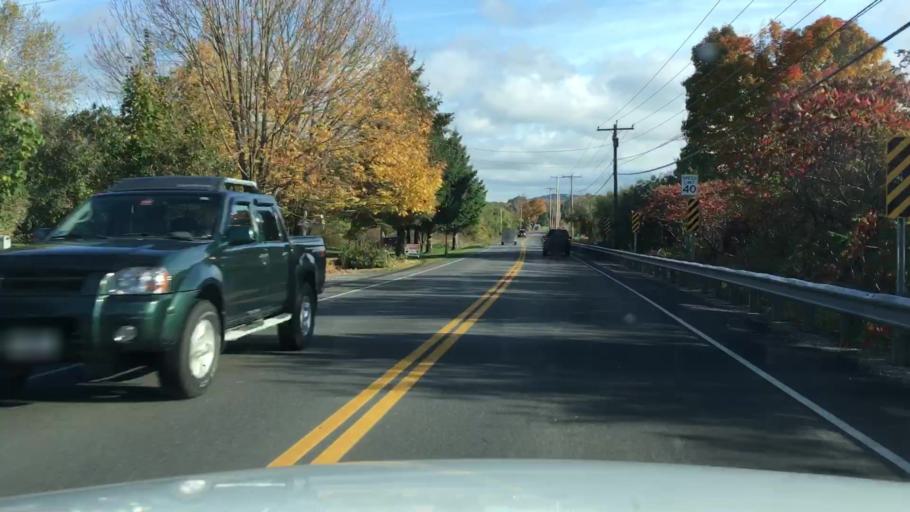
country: US
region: Maine
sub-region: Knox County
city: Rockland
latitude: 44.1035
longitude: -69.1407
